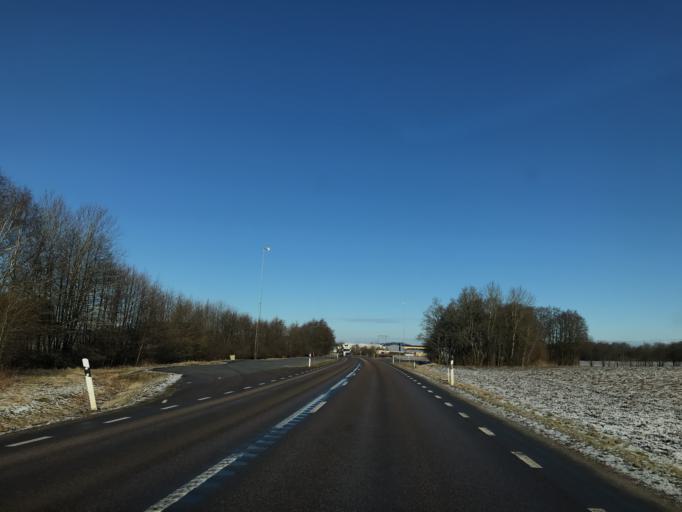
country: SE
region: Skane
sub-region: Bjuvs Kommun
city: Billesholm
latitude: 56.0407
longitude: 12.9697
